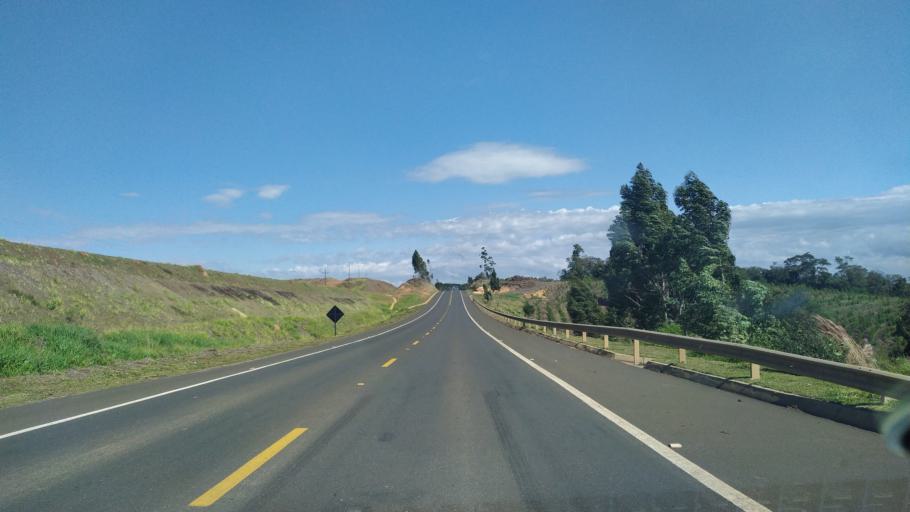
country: BR
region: Parana
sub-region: Ortigueira
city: Ortigueira
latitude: -24.2829
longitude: -50.8100
